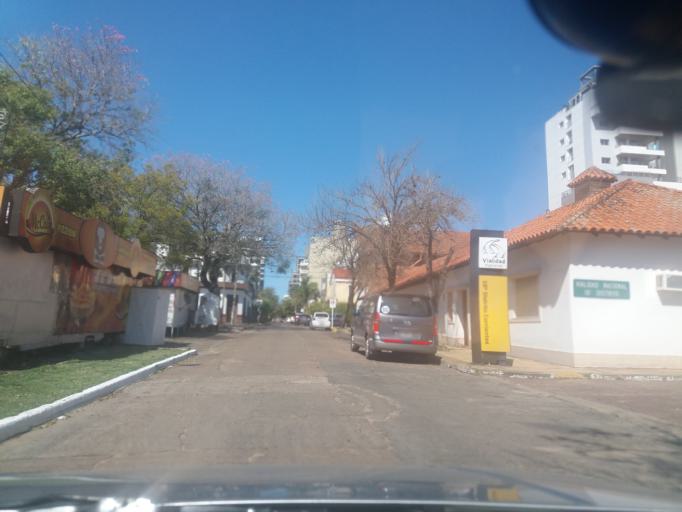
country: AR
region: Corrientes
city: Corrientes
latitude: -27.4651
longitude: -58.8466
